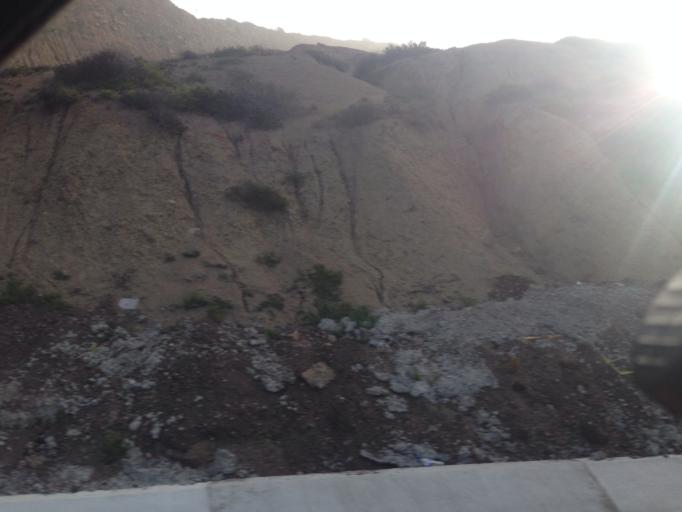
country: MX
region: Baja California
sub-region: Playas de Rosarito
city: Santa Anita
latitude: 32.1277
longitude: -116.8839
